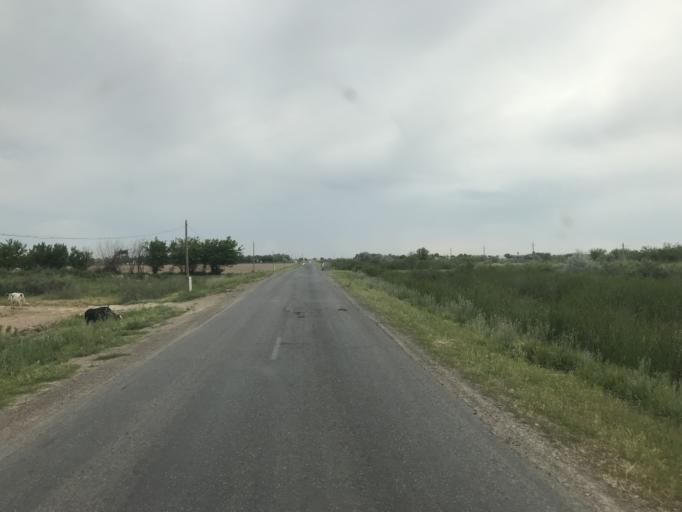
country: KZ
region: Ongtustik Qazaqstan
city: Asykata
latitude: 40.9206
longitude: 68.3997
